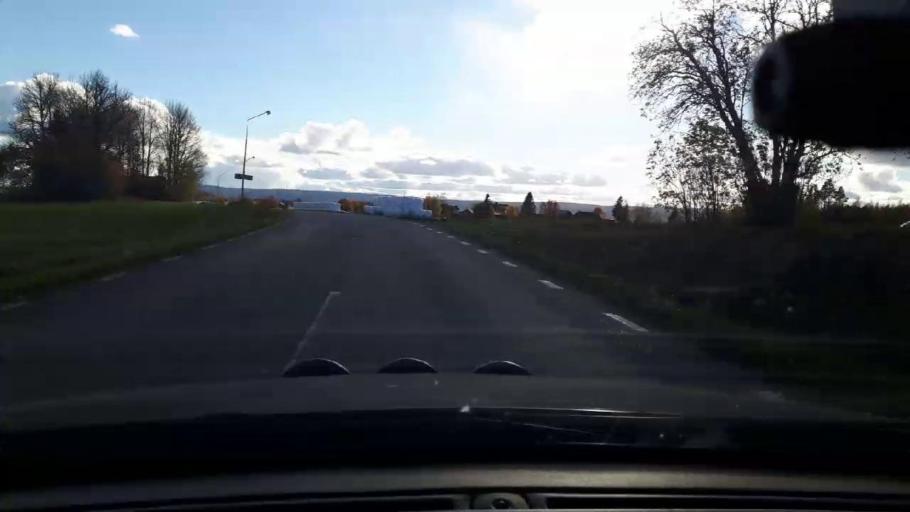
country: SE
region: Jaemtland
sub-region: Bergs Kommun
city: Hoverberg
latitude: 63.0127
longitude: 14.3414
